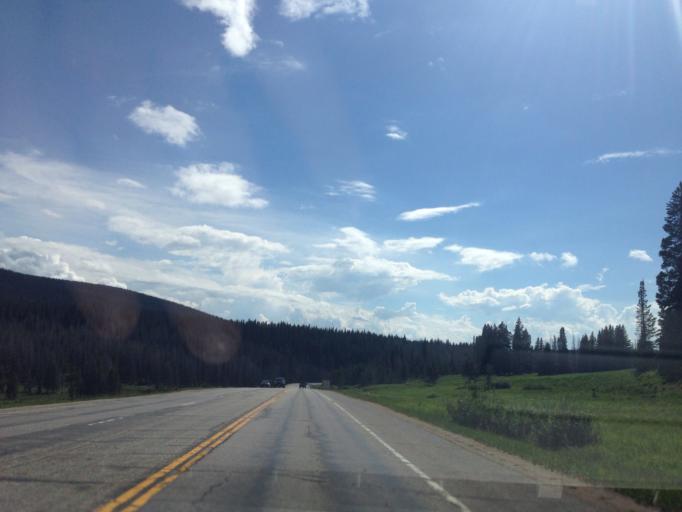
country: US
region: Colorado
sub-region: Routt County
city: Steamboat Springs
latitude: 40.3853
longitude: -106.6820
